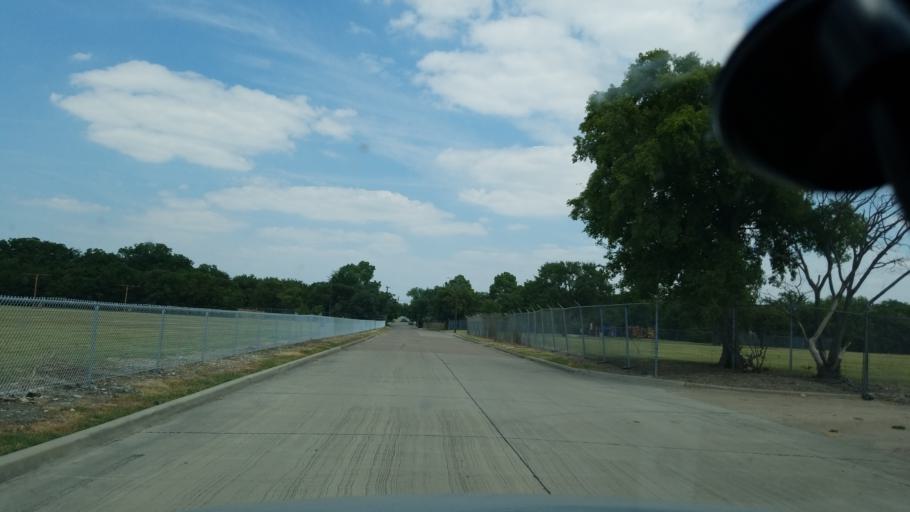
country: US
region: Texas
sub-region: Dallas County
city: Grand Prairie
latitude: 32.7515
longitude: -96.9686
